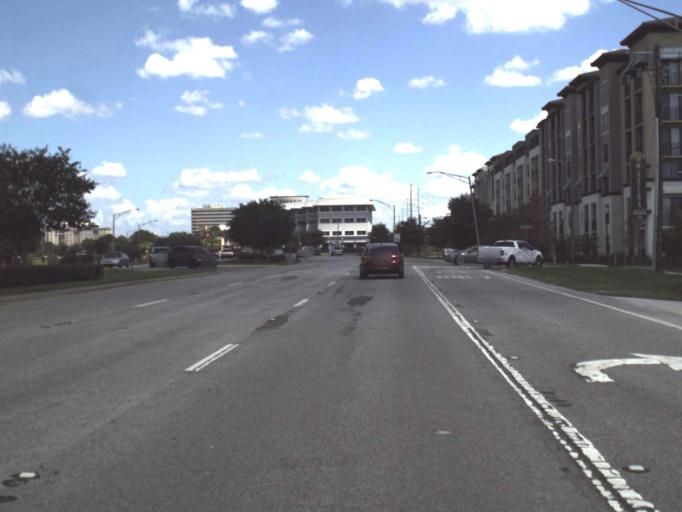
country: US
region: Florida
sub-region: Hillsborough County
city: Egypt Lake-Leto
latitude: 27.9596
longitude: -82.5227
